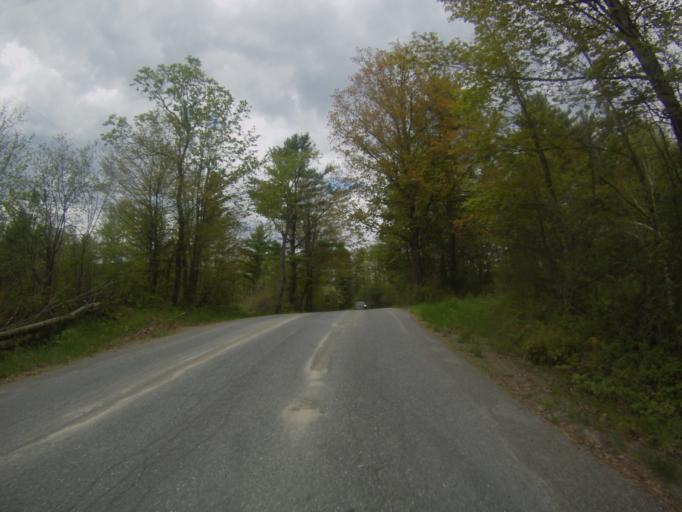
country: US
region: New York
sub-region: Essex County
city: Ticonderoga
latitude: 43.9302
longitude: -73.5058
